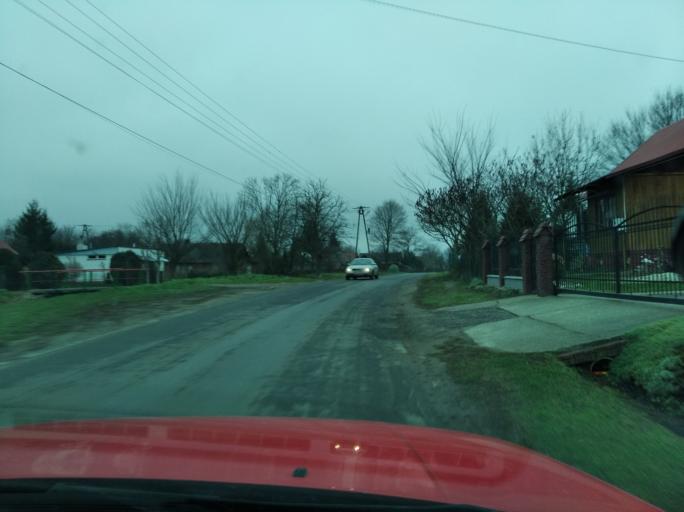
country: PL
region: Subcarpathian Voivodeship
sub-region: Powiat przeworski
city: Rozborz
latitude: 50.0621
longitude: 22.5402
